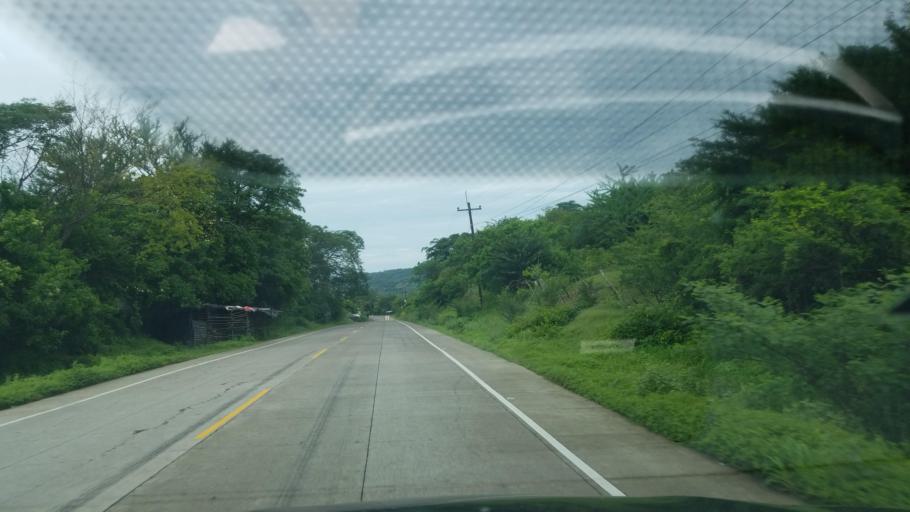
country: HN
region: Choluteca
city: Pespire
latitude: 13.6614
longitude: -87.3620
